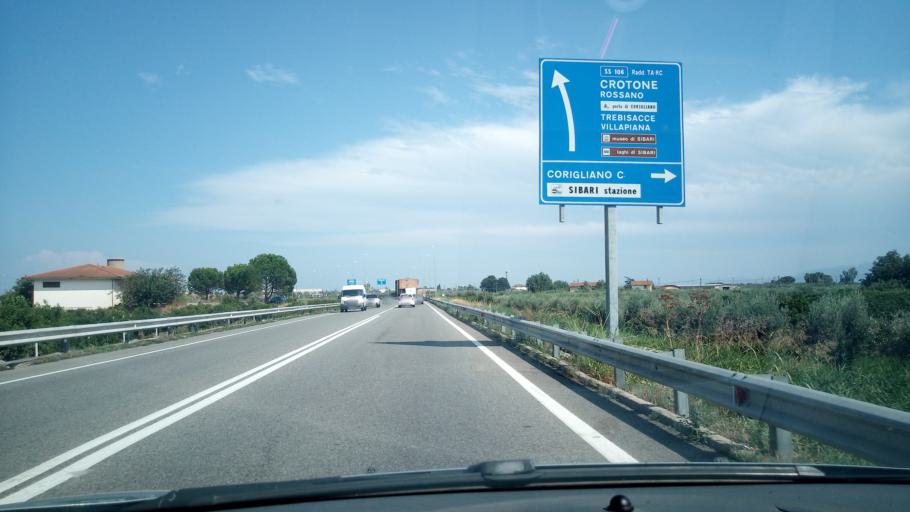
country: IT
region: Calabria
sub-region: Provincia di Cosenza
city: Sibari
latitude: 39.7230
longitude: 16.4414
